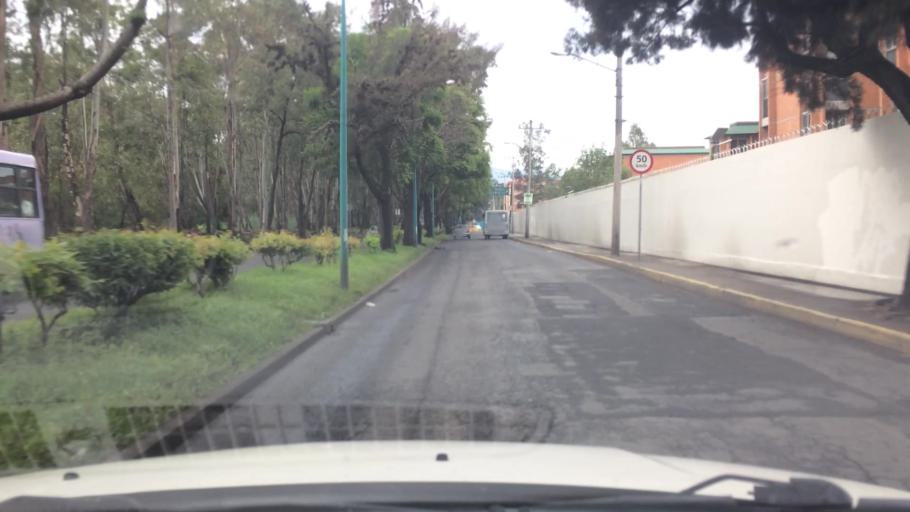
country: MX
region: Mexico City
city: Xochimilco
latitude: 19.2986
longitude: -99.1010
